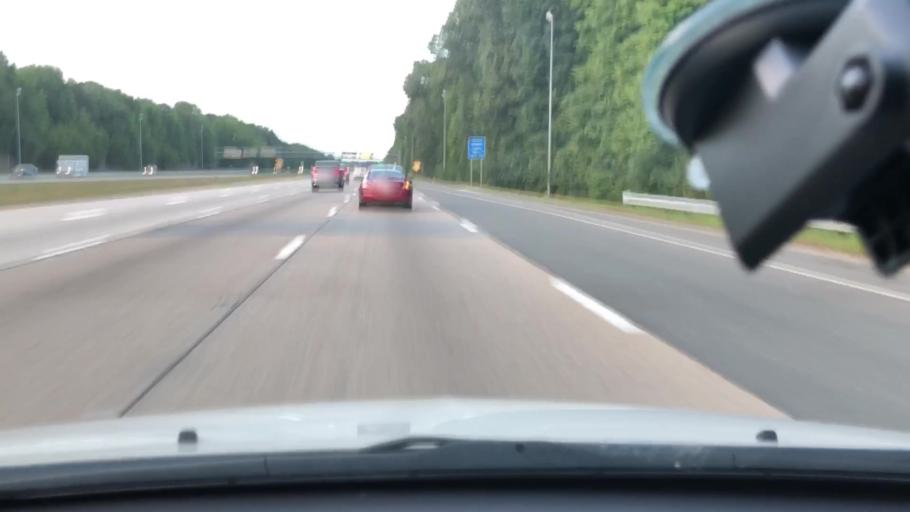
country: US
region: Virginia
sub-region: City of Chesapeake
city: Chesapeake
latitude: 36.7918
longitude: -76.2164
